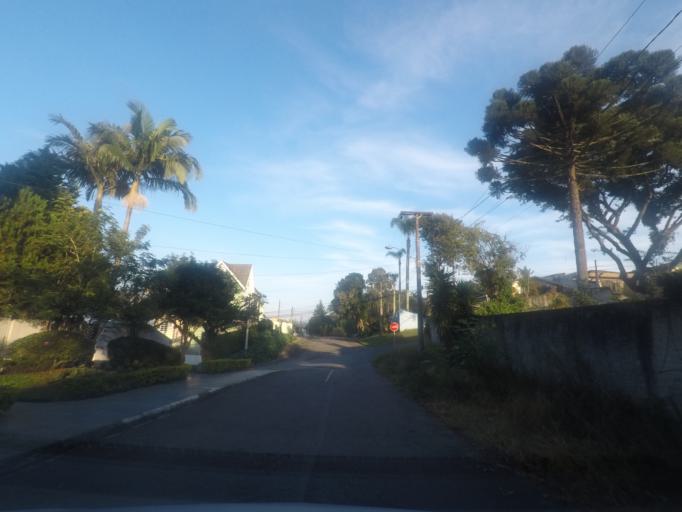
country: BR
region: Parana
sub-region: Curitiba
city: Curitiba
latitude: -25.3966
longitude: -49.2631
